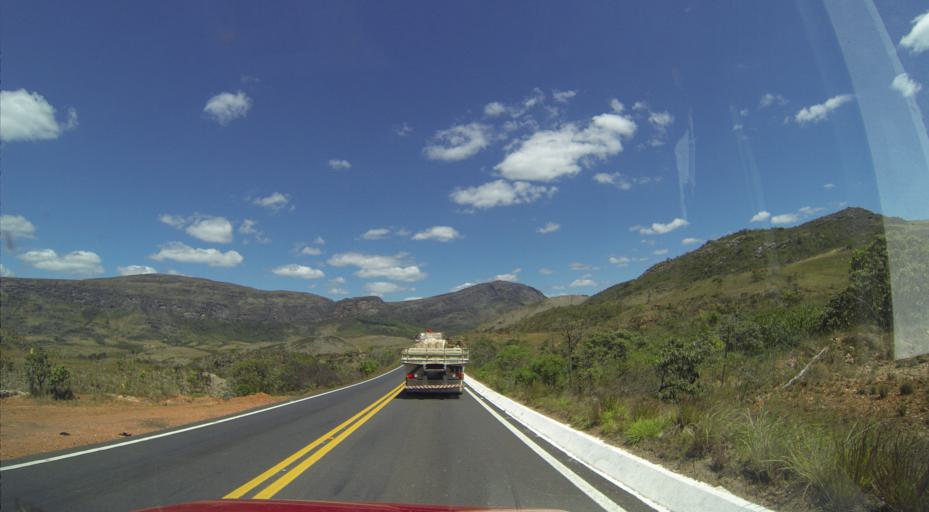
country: BR
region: Minas Gerais
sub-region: Conceicao Do Mato Dentro
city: Conceicao do Mato Dentro
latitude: -19.2879
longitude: -43.5613
